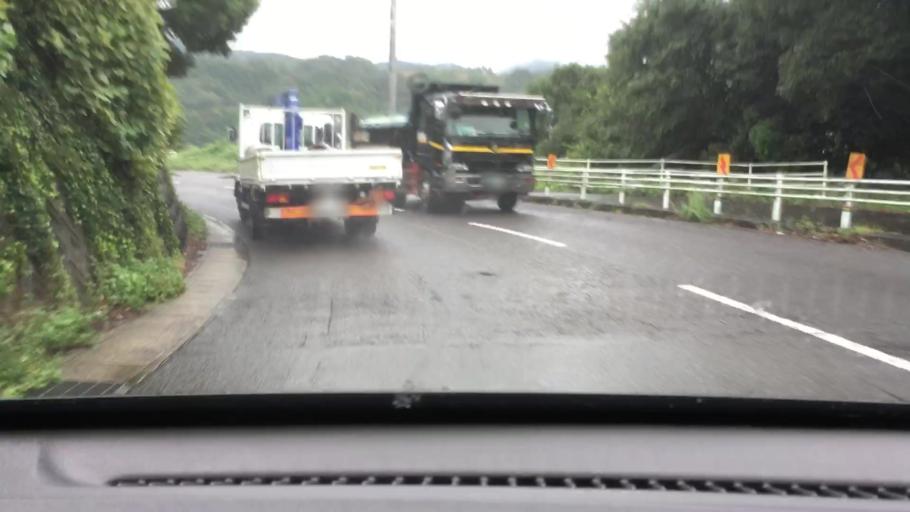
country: JP
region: Nagasaki
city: Togitsu
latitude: 32.8558
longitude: 129.7808
